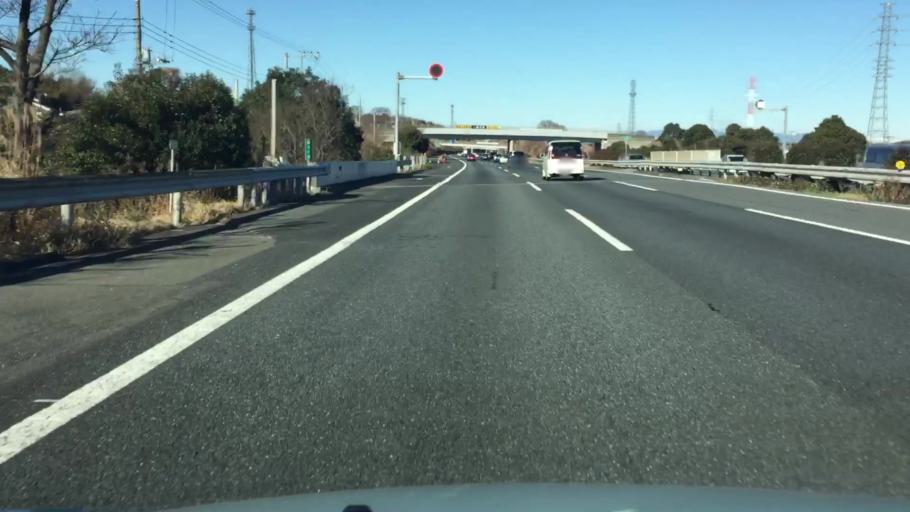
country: JP
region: Saitama
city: Yorii
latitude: 36.1620
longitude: 139.2076
